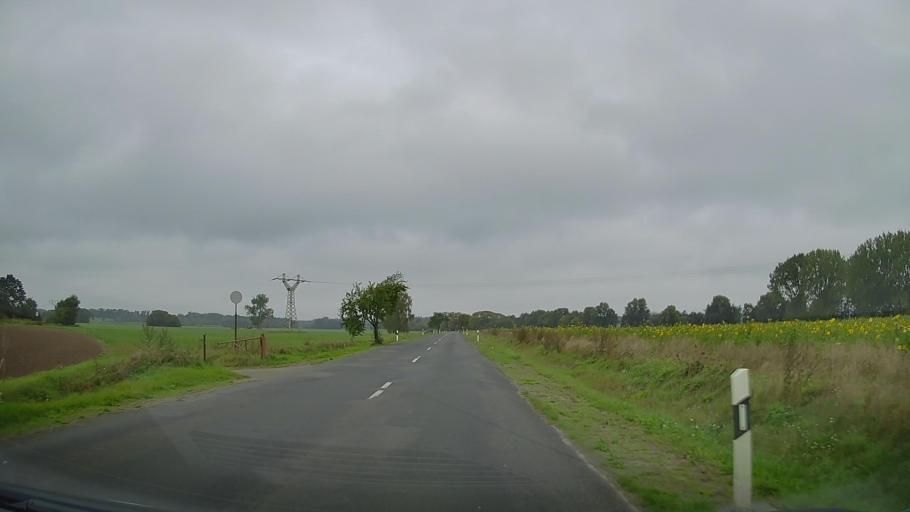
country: DE
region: Mecklenburg-Vorpommern
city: Guestrow
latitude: 53.8091
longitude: 12.1439
